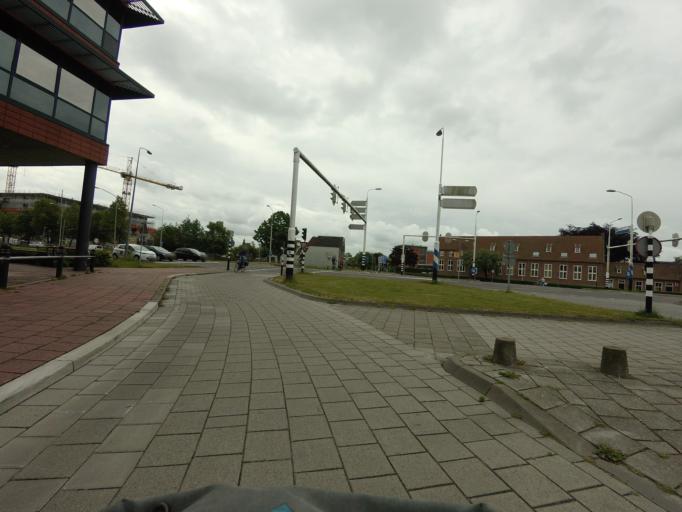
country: NL
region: North Holland
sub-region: Gemeente Hoorn
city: Hoorn
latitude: 52.6482
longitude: 5.0469
